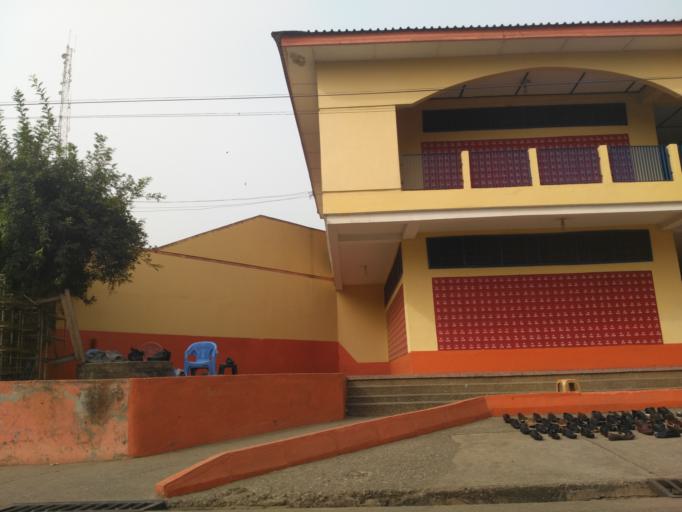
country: GH
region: Ashanti
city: Kumasi
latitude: 6.6908
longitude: -1.6227
